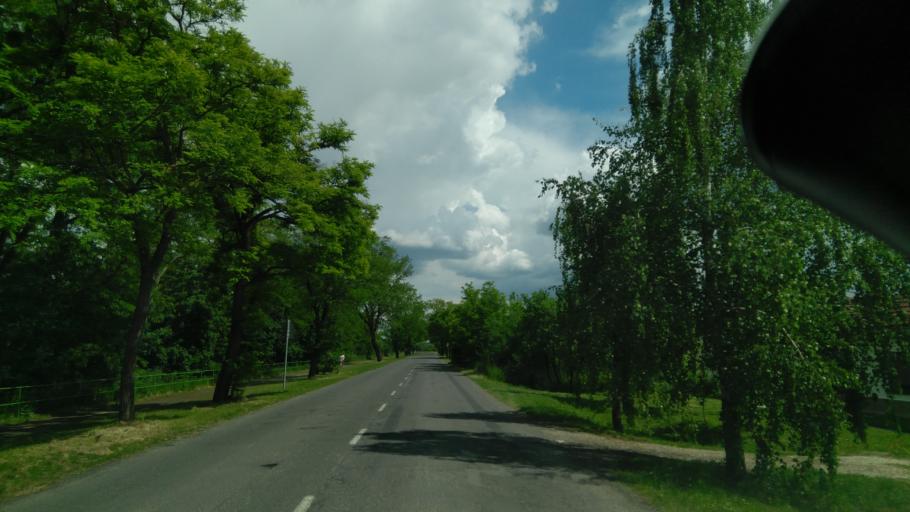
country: HU
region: Bekes
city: Korosladany
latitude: 46.9708
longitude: 21.0651
